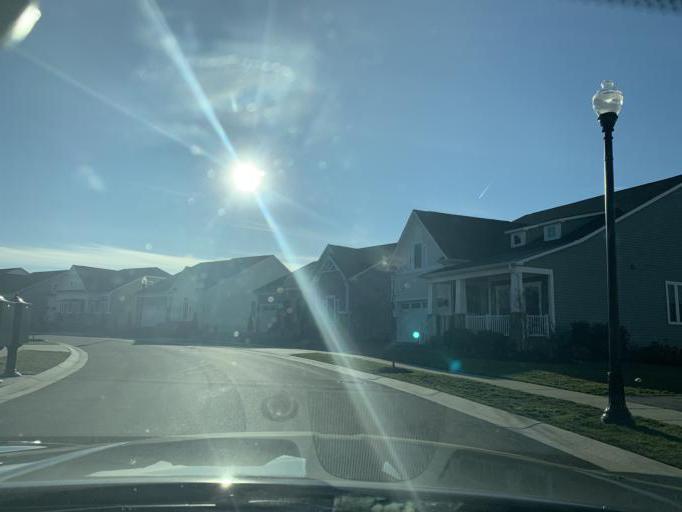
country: US
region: Maryland
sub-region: Anne Arundel County
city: Crofton
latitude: 39.0268
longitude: -76.7234
